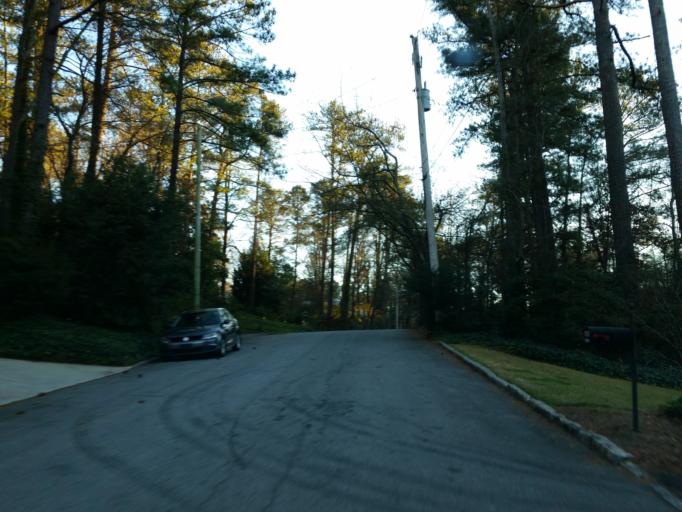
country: US
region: Georgia
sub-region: Cobb County
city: Vinings
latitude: 33.8440
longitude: -84.4226
